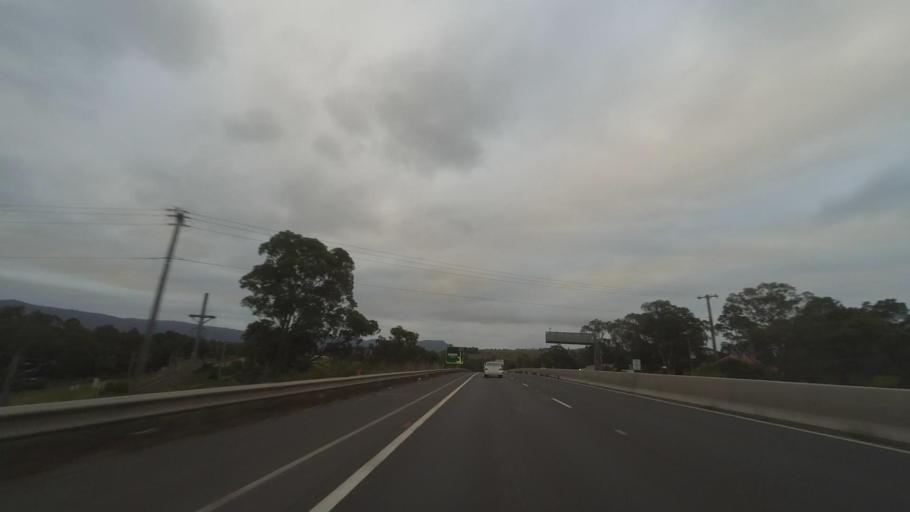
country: AU
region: New South Wales
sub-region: Shellharbour
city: Albion Park Rail
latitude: -34.5372
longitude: 150.7853
